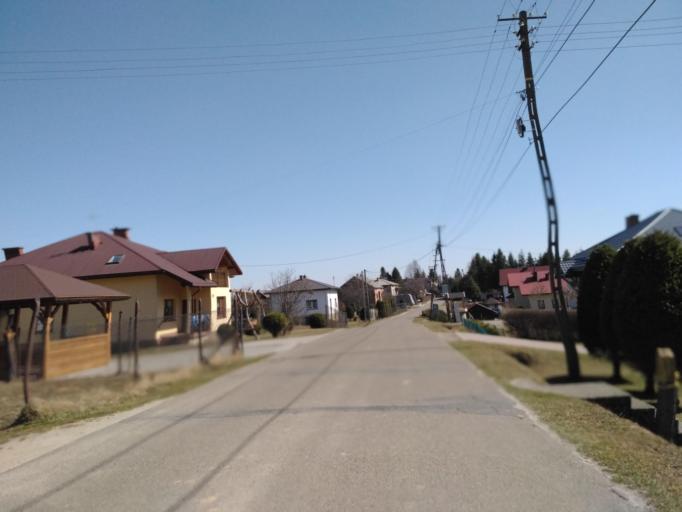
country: PL
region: Subcarpathian Voivodeship
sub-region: Powiat brzozowski
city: Orzechowka
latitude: 49.7352
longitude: 21.9180
